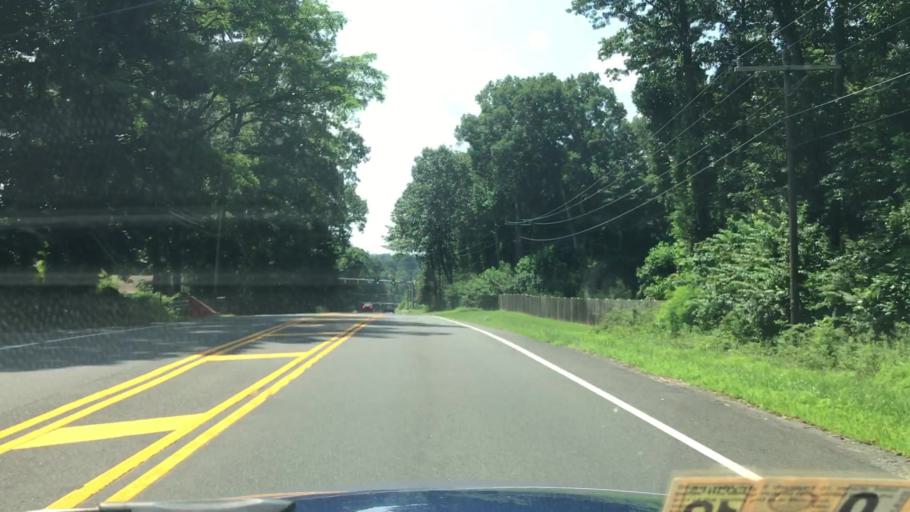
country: US
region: Virginia
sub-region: Fairfax County
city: Oakton
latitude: 38.9043
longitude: -77.3032
